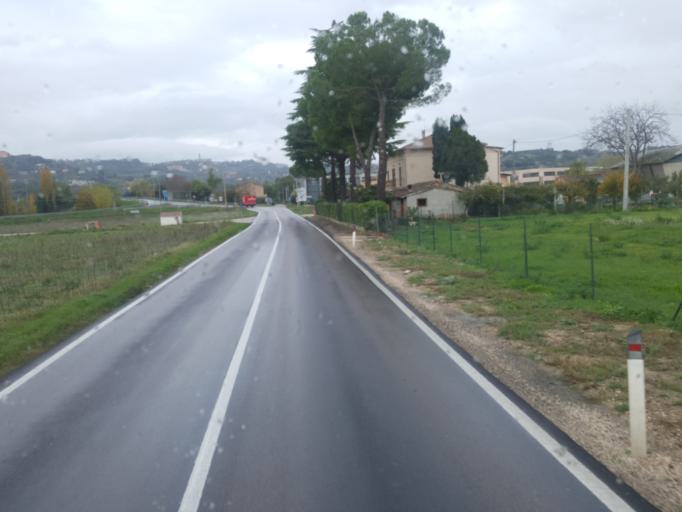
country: IT
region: Umbria
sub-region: Provincia di Perugia
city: San Martino in Campo
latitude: 43.0747
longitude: 12.4242
